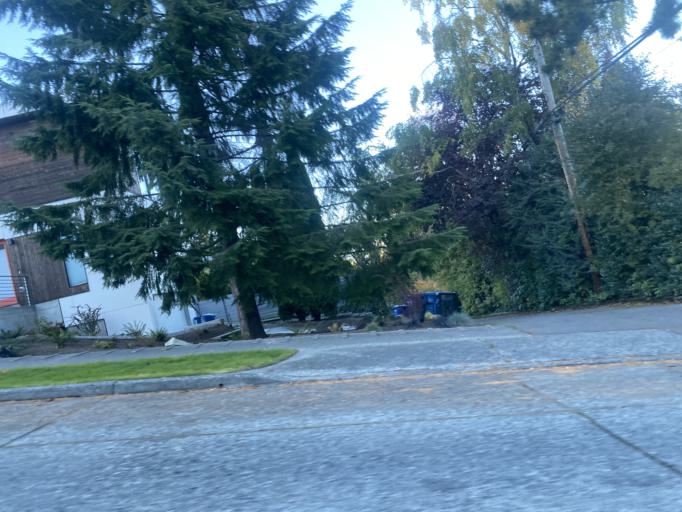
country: US
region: Washington
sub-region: King County
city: Seattle
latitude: 47.6540
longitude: -122.4032
